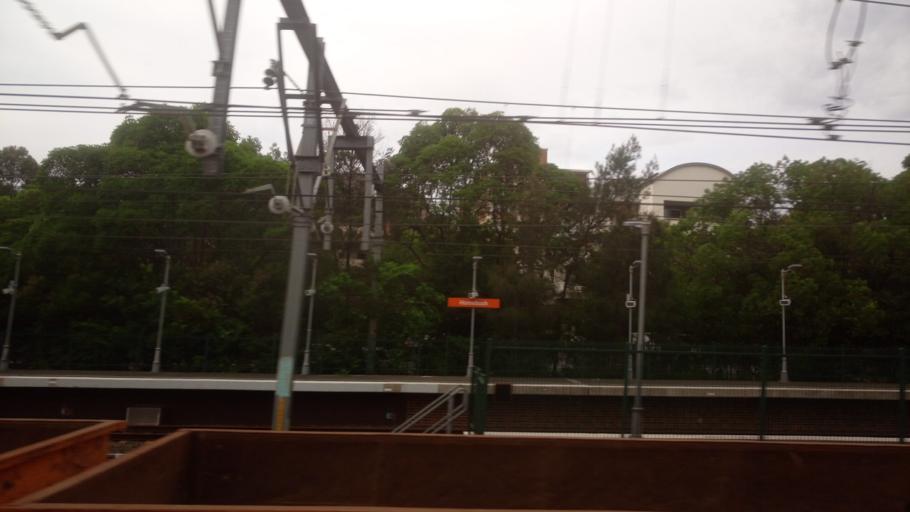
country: AU
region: New South Wales
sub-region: Strathfield
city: Homebush
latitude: -33.8673
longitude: 151.0877
